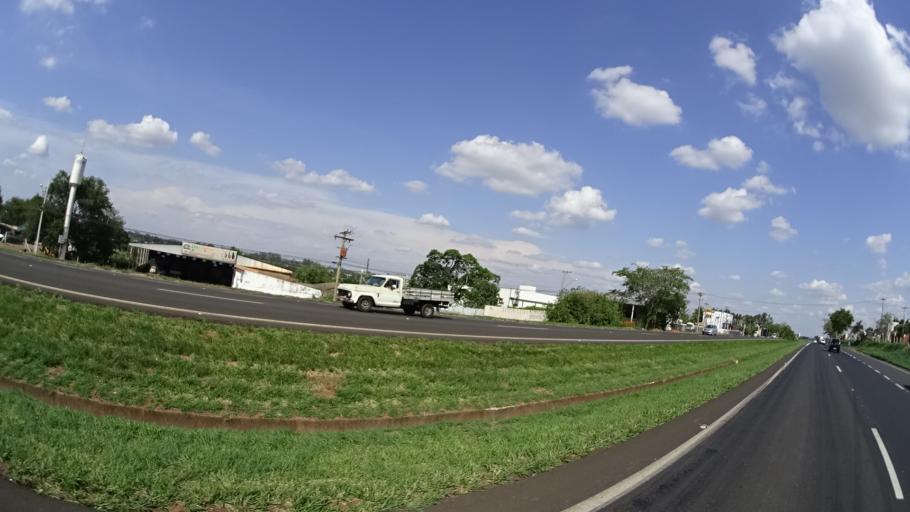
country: BR
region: Sao Paulo
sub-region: Sao Jose Do Rio Preto
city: Sao Jose do Rio Preto
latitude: -20.8533
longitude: -49.3418
